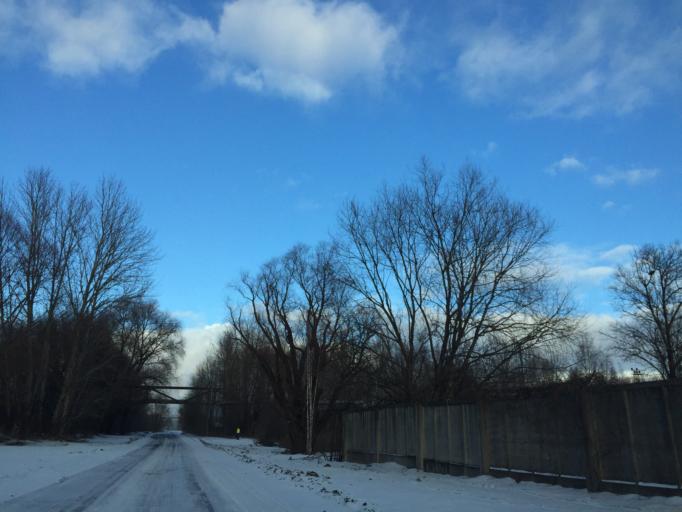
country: LV
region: Riga
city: Riga
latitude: 56.9840
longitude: 24.1093
